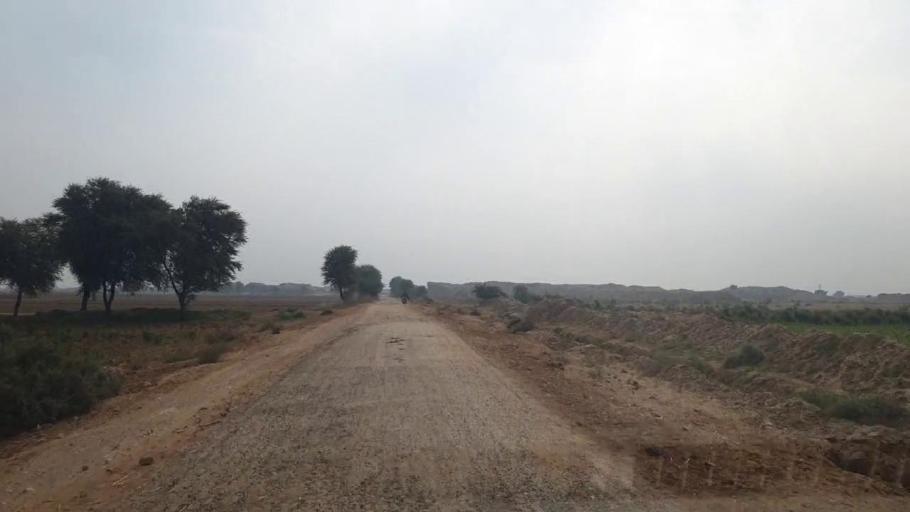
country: PK
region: Sindh
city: Sann
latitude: 26.0197
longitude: 68.1438
